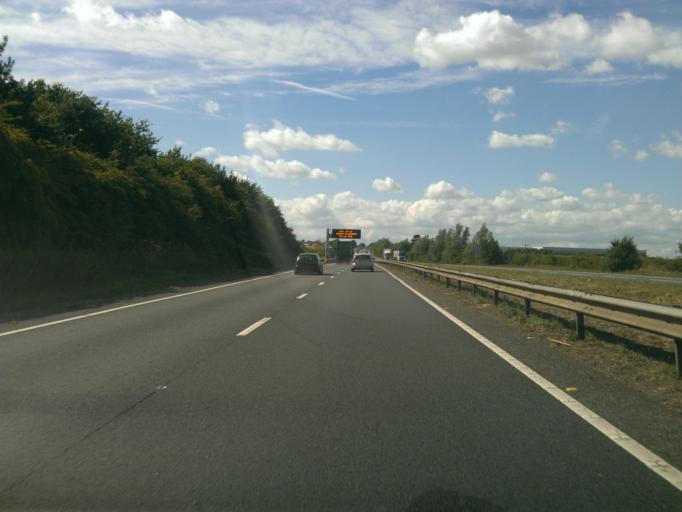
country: GB
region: England
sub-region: Northamptonshire
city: Thrapston
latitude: 52.3875
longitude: -0.4997
